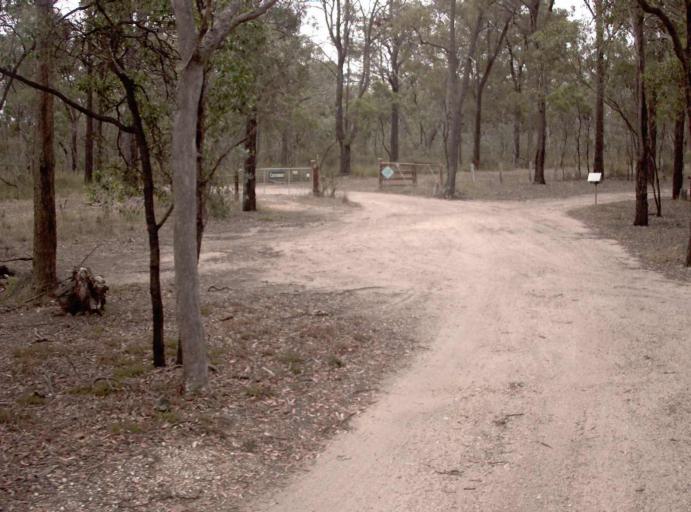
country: AU
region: Victoria
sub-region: Wellington
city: Heyfield
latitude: -37.9546
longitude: 146.7702
